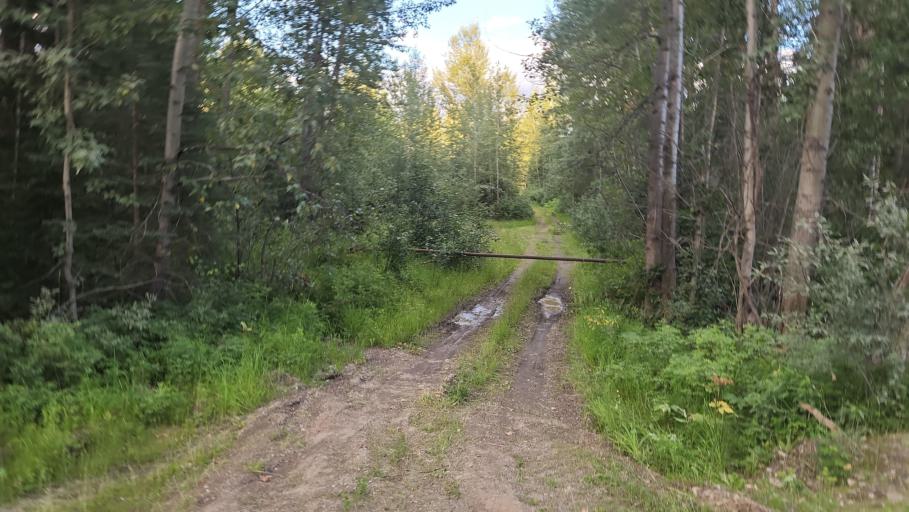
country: CA
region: British Columbia
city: Quesnel
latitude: 53.0167
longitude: -122.0817
